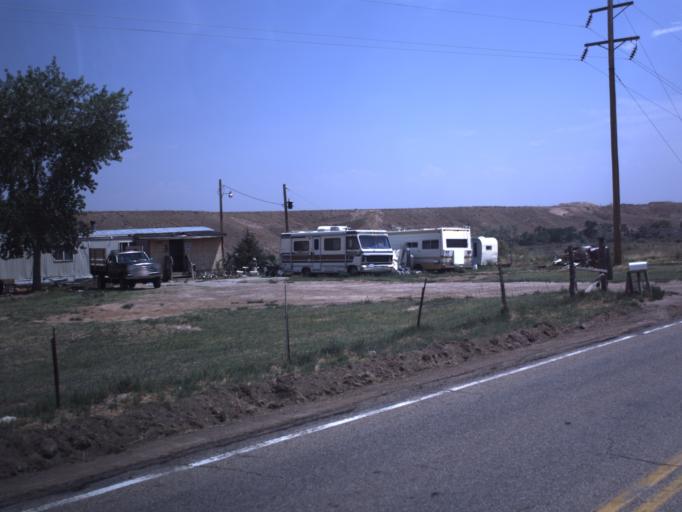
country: US
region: Utah
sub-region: Duchesne County
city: Roosevelt
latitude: 40.3473
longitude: -110.0283
